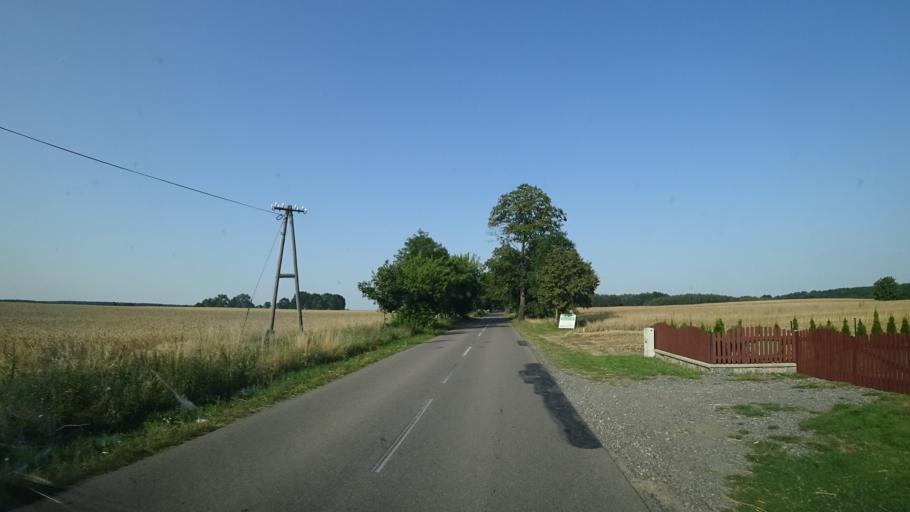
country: PL
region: Pomeranian Voivodeship
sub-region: Powiat czluchowski
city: Przechlewo
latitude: 53.8104
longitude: 17.3506
